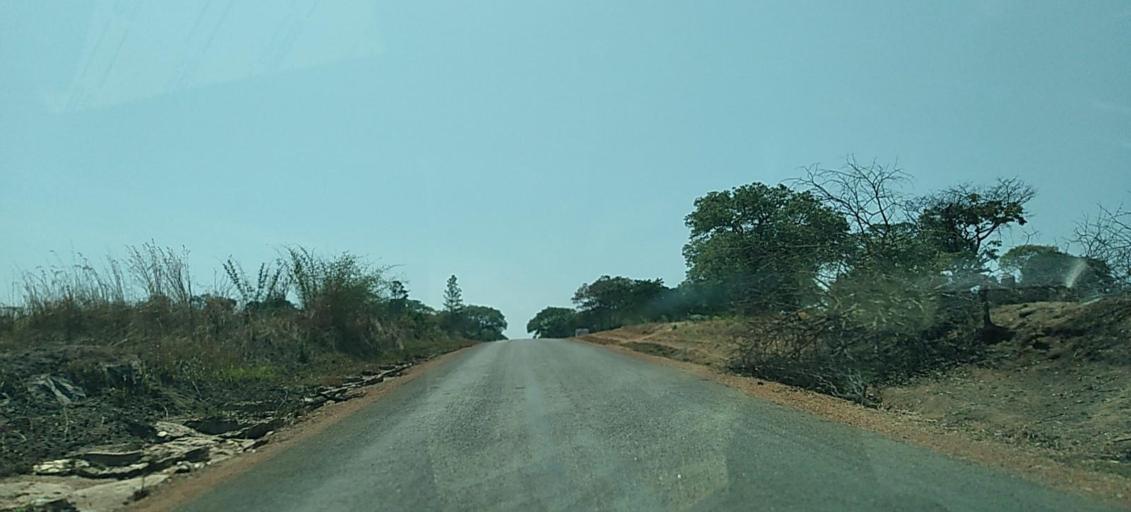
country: ZM
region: North-Western
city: Solwezi
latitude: -12.2740
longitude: 25.6674
